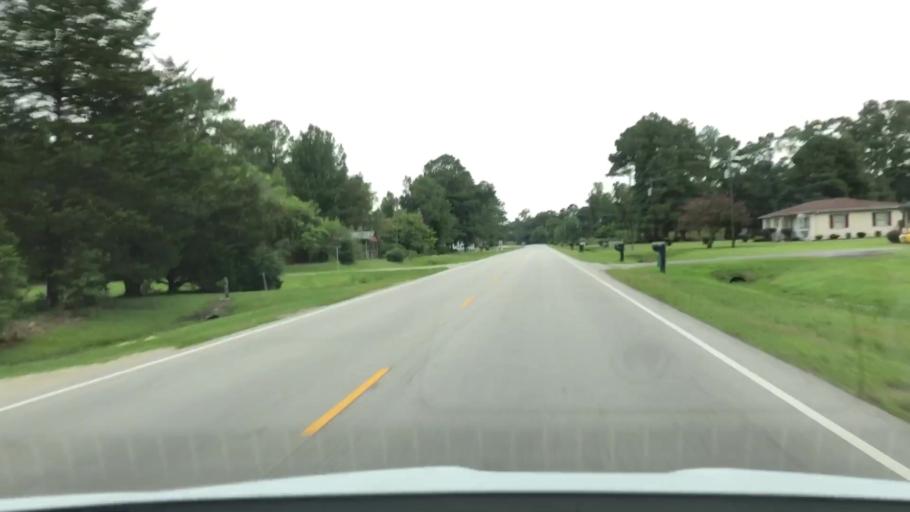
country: US
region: North Carolina
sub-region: Jones County
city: Trenton
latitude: 35.0234
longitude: -77.3059
